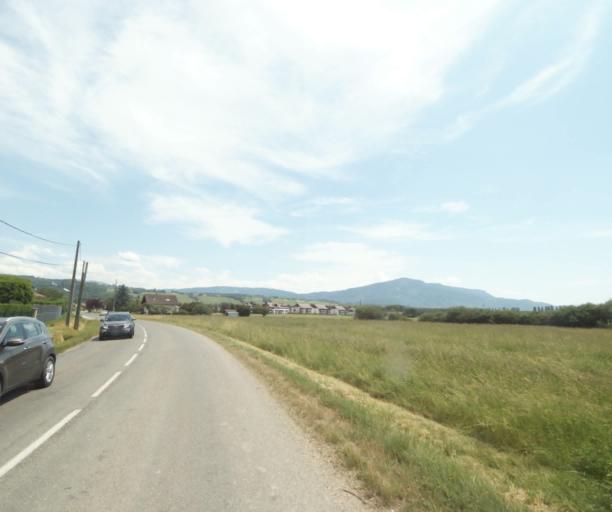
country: FR
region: Rhone-Alpes
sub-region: Departement de la Haute-Savoie
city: Douvaine
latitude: 46.3080
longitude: 6.2890
